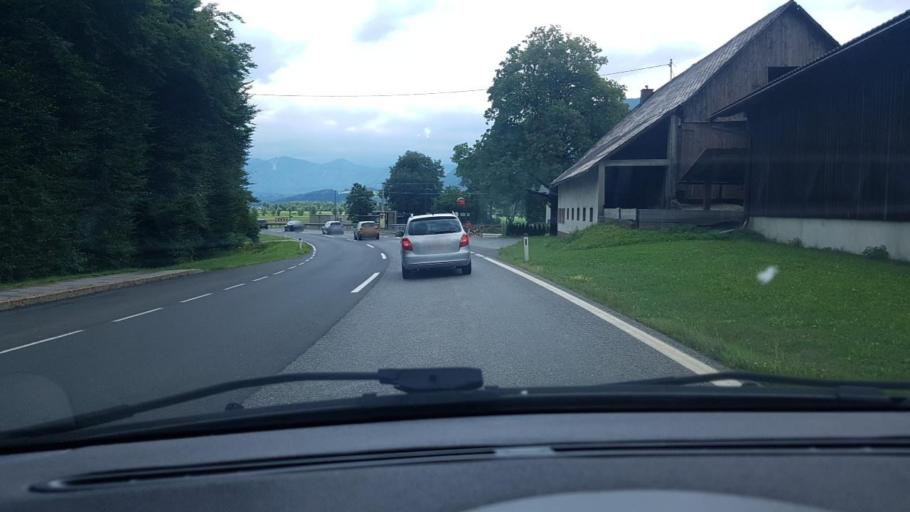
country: AT
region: Carinthia
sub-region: Politischer Bezirk Villach Land
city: Feistritz an der Gail
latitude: 46.5961
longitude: 13.5715
